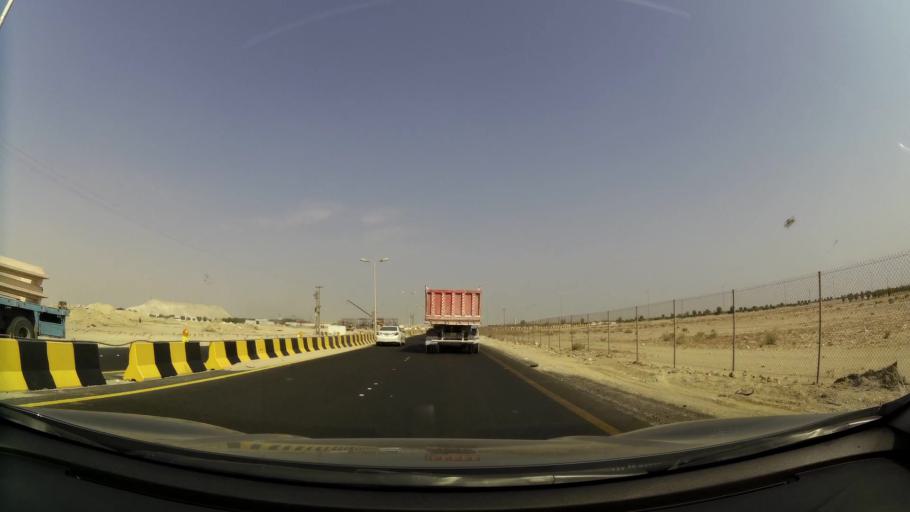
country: KW
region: Al Ahmadi
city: Al Fahahil
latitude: 28.9700
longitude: 48.1279
